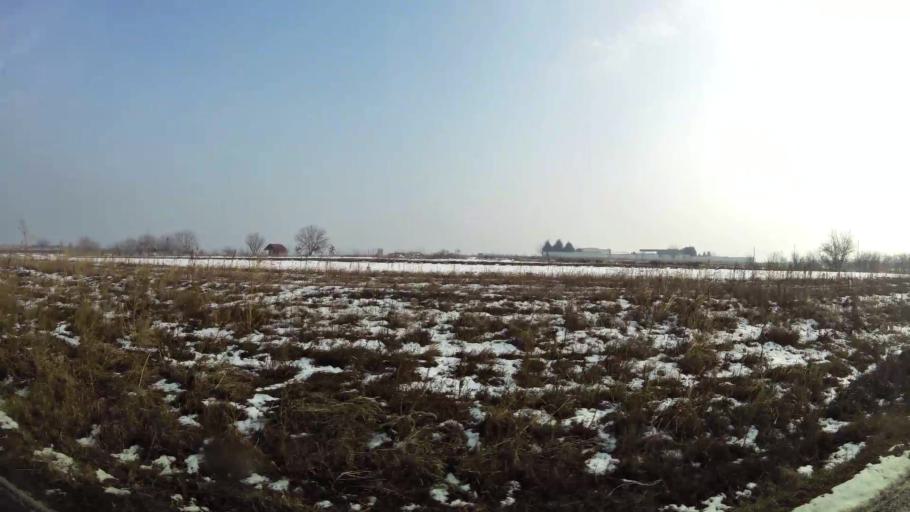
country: MK
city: Kadino
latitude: 41.9715
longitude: 21.6057
